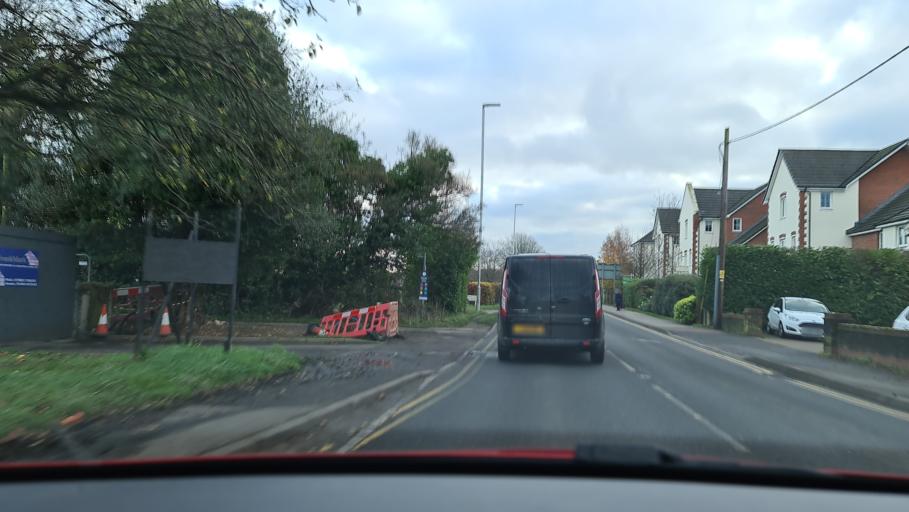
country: GB
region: England
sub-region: Buckinghamshire
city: High Wycombe
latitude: 51.6514
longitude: -0.7115
